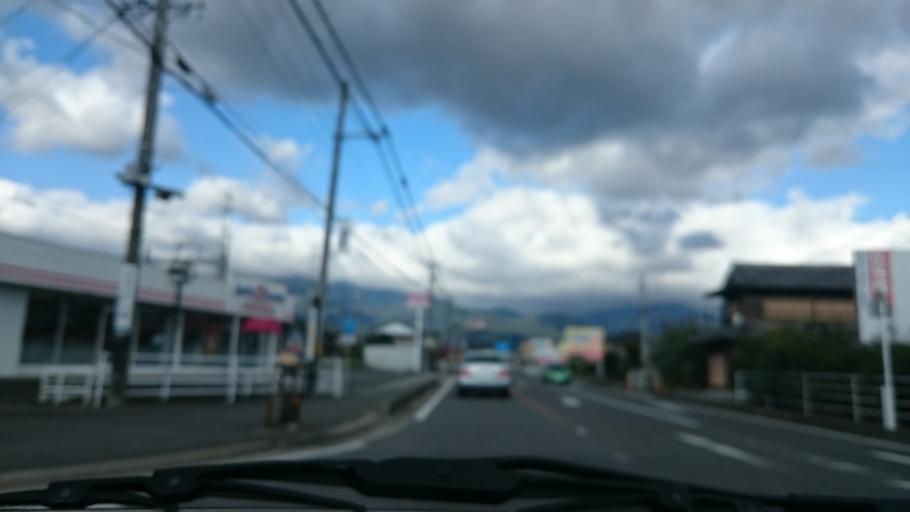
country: JP
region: Mie
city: Komono
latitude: 35.0050
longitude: 136.5260
